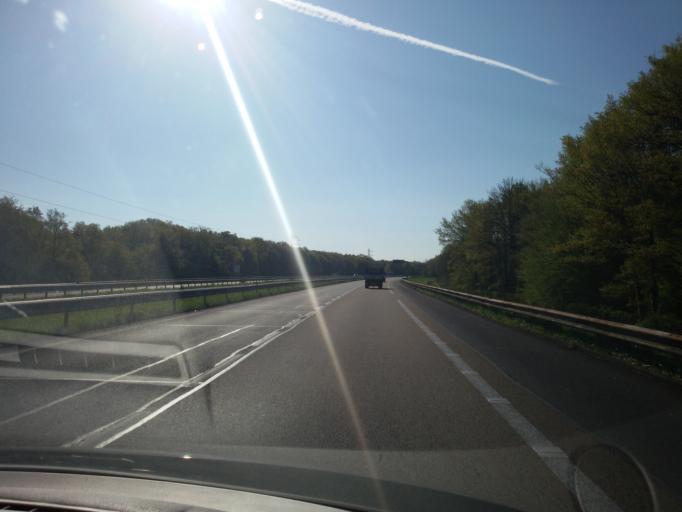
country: FR
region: Centre
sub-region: Departement du Loiret
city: Courtenay
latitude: 48.1088
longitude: 3.0097
